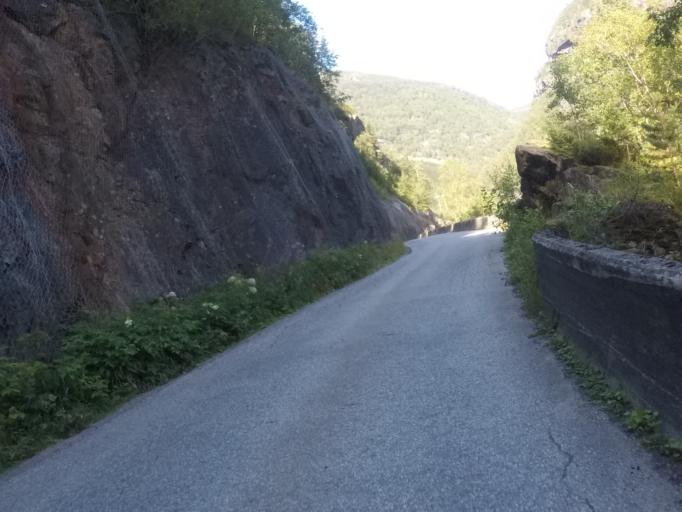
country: NO
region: Hordaland
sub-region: Odda
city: Odda
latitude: 60.1253
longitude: 6.5970
